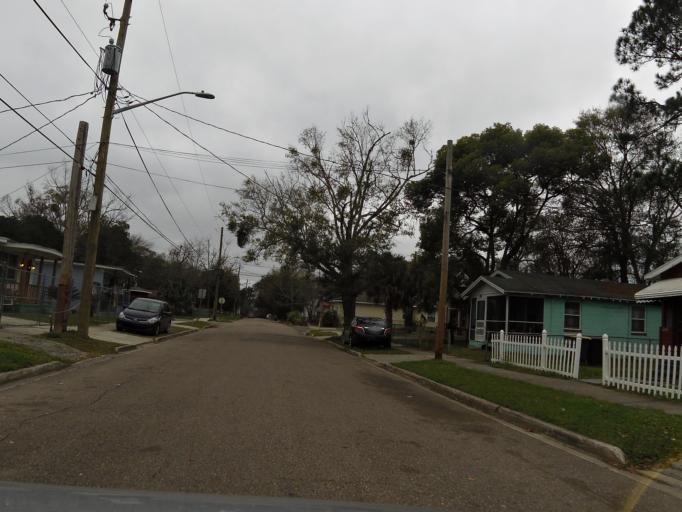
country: US
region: Florida
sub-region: Duval County
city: Jacksonville
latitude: 30.3594
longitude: -81.6877
